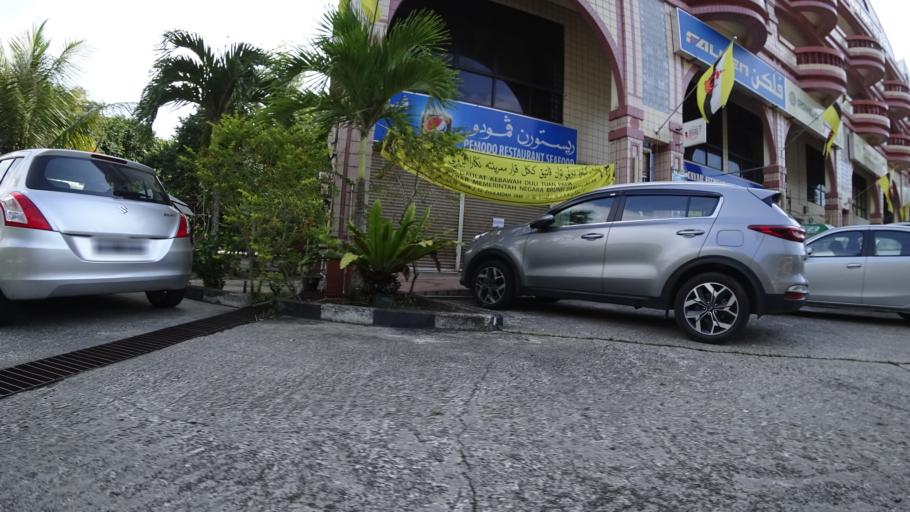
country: BN
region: Brunei and Muara
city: Bandar Seri Begawan
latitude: 4.8680
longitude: 114.9010
